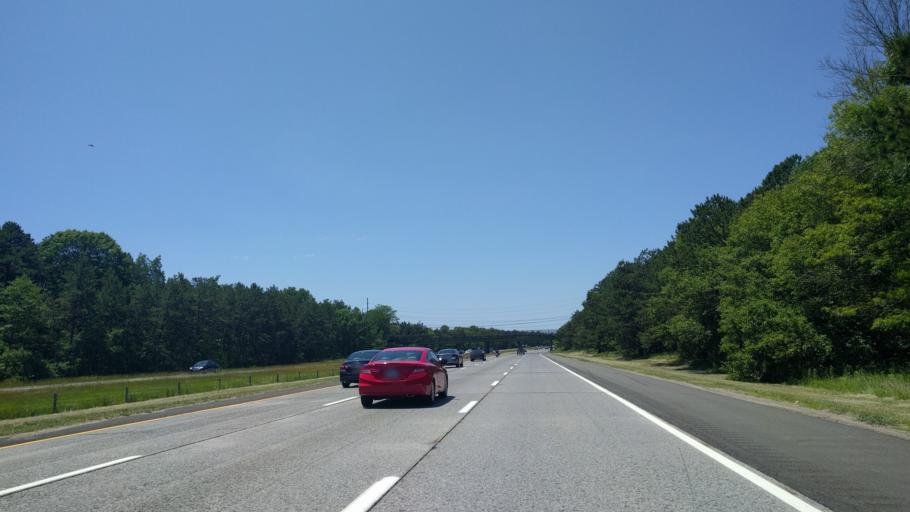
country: US
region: New York
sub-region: Suffolk County
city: Manorville
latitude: 40.8560
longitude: -72.8405
